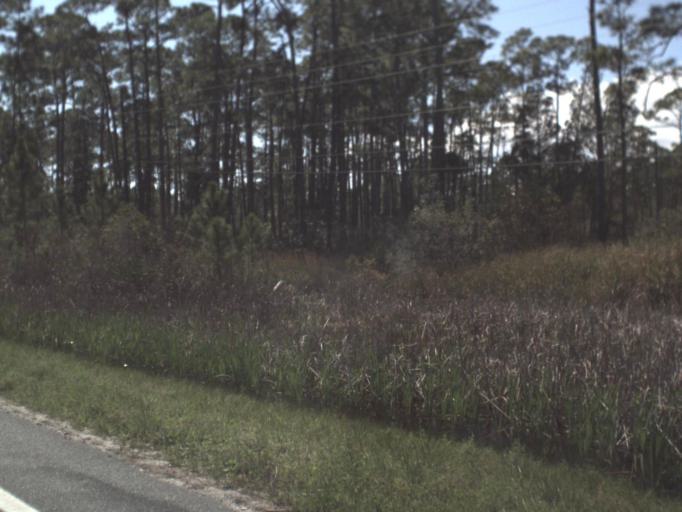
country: US
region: Florida
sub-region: Wakulla County
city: Crawfordville
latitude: 30.0088
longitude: -84.3953
